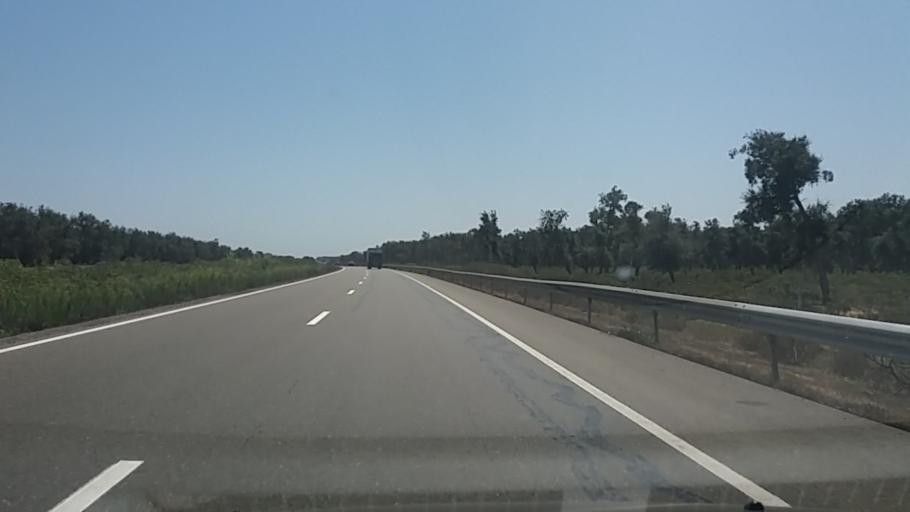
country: MA
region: Rabat-Sale-Zemmour-Zaer
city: Sale
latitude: 34.0615
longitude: -6.7118
